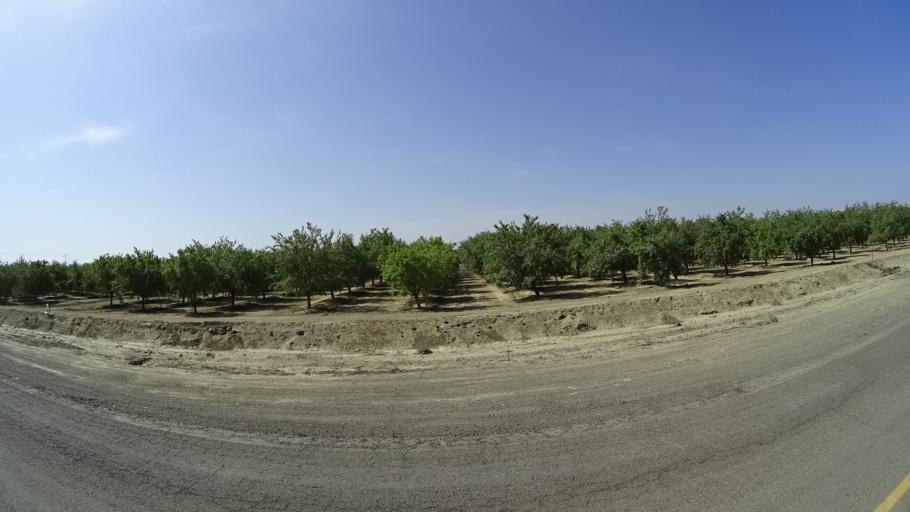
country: US
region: California
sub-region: Kings County
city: Kettleman City
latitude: 36.0364
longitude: -119.9616
